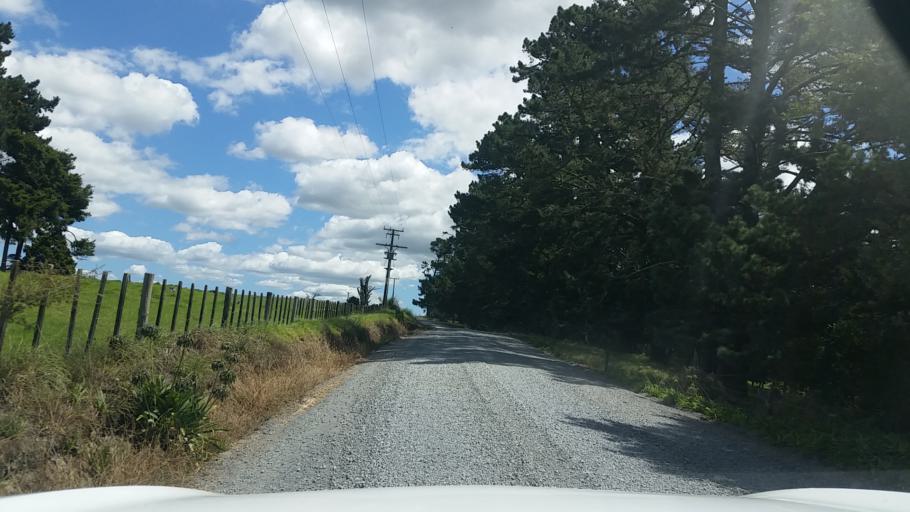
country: NZ
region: Northland
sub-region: Whangarei
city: Maungatapere
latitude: -35.6644
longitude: 174.1808
